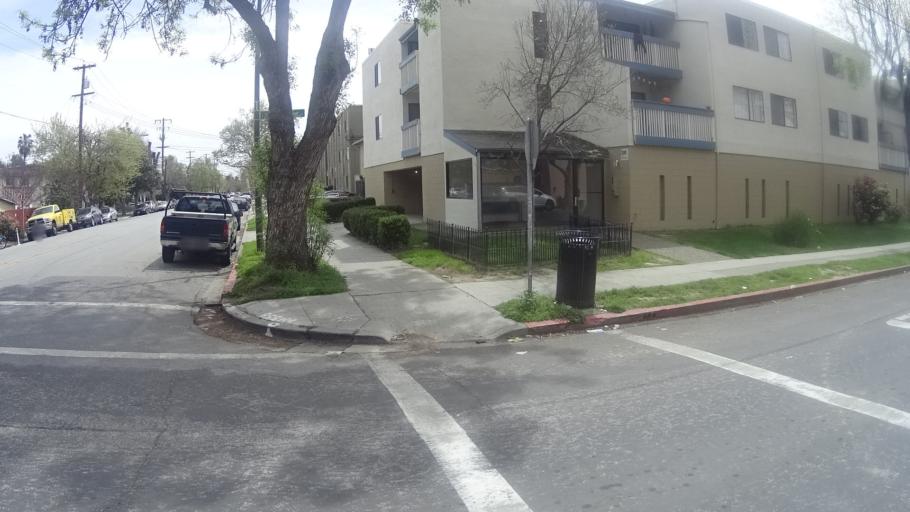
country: US
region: California
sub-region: Santa Clara County
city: San Jose
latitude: 37.3340
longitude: -121.8776
